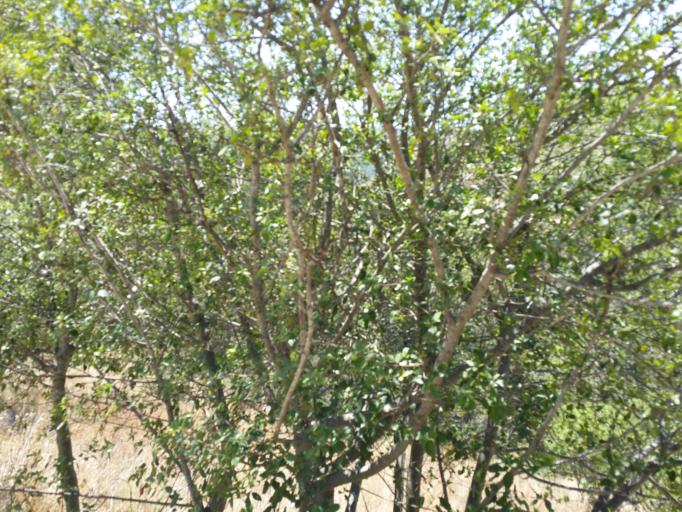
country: IT
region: Sicily
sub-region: Provincia di Siracusa
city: Sortino
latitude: 37.1422
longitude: 15.0329
